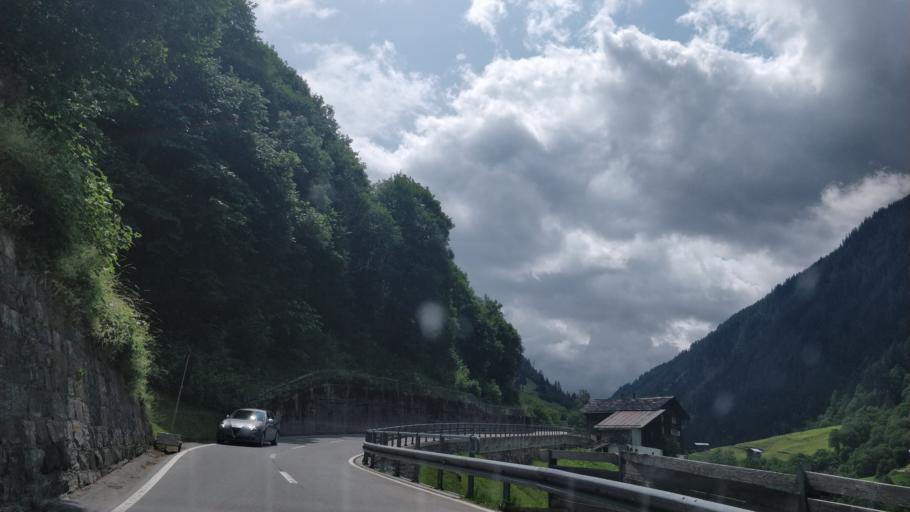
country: CH
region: Grisons
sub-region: Surselva District
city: Ilanz
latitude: 46.6609
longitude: 9.1901
